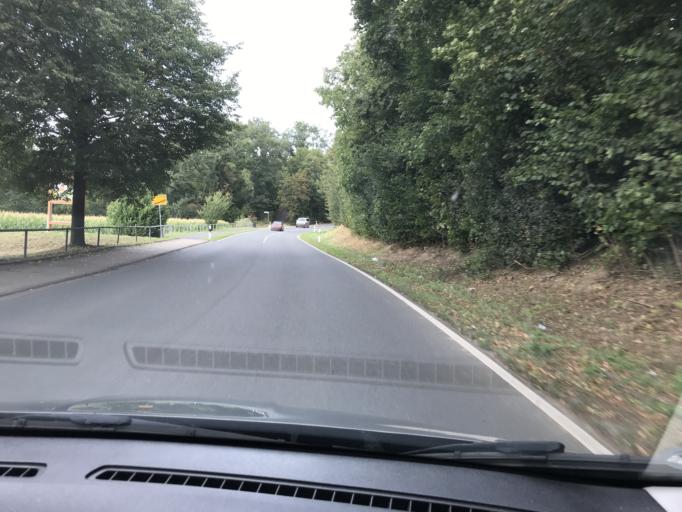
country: DE
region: Hesse
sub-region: Regierungsbezirk Darmstadt
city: Schaafheim
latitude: 49.9147
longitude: 8.9763
